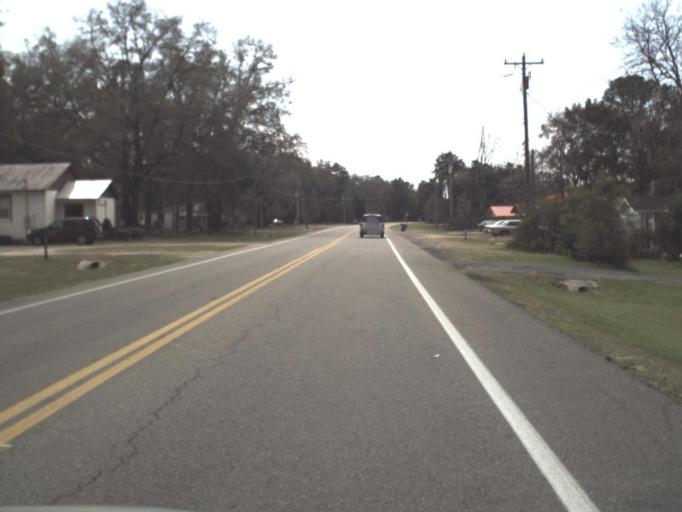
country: US
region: Florida
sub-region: Liberty County
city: Bristol
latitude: 30.4421
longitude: -84.9725
